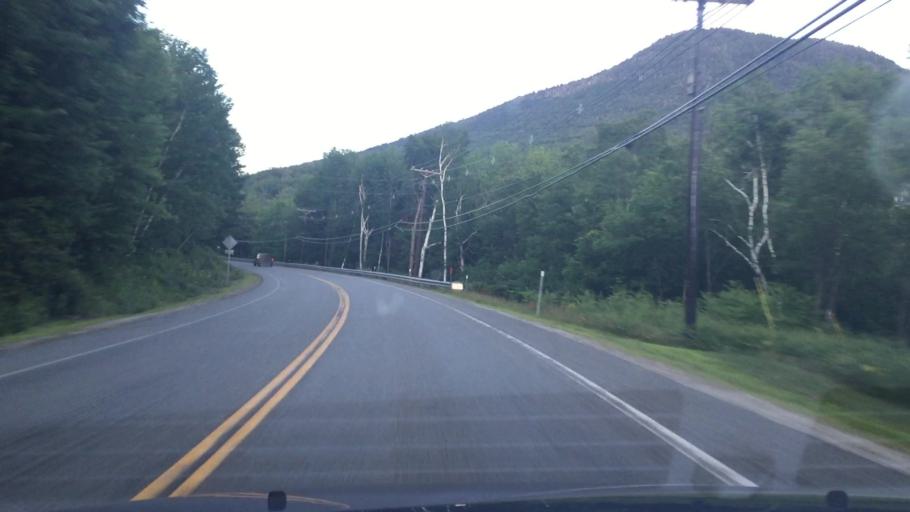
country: US
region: New Hampshire
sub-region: Grafton County
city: Woodstock
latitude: 44.0578
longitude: -71.6297
